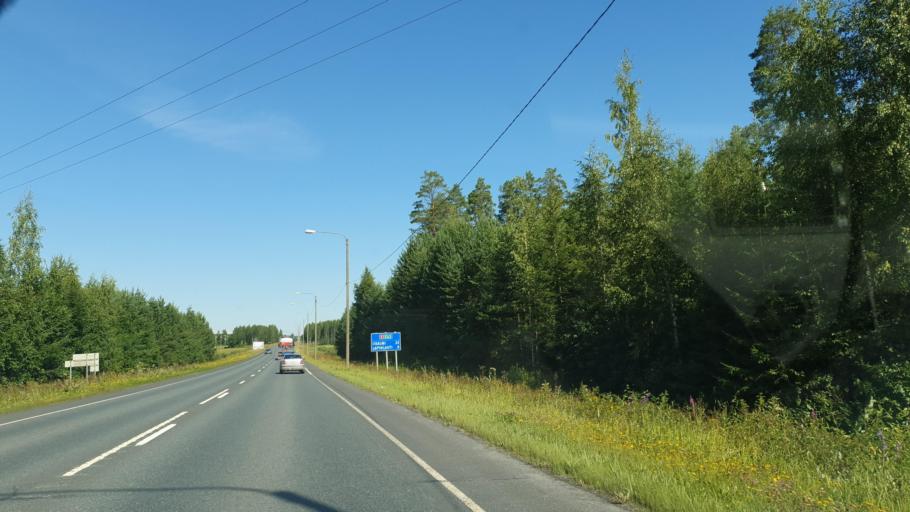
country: FI
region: Northern Savo
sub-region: Ylae-Savo
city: Lapinlahti
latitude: 63.3096
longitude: 27.4490
